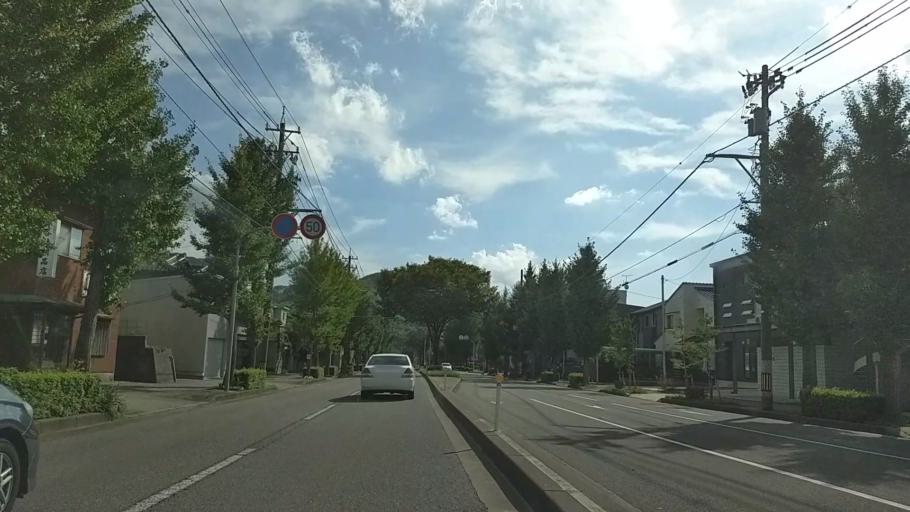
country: JP
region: Ishikawa
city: Nonoichi
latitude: 36.5328
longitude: 136.6538
